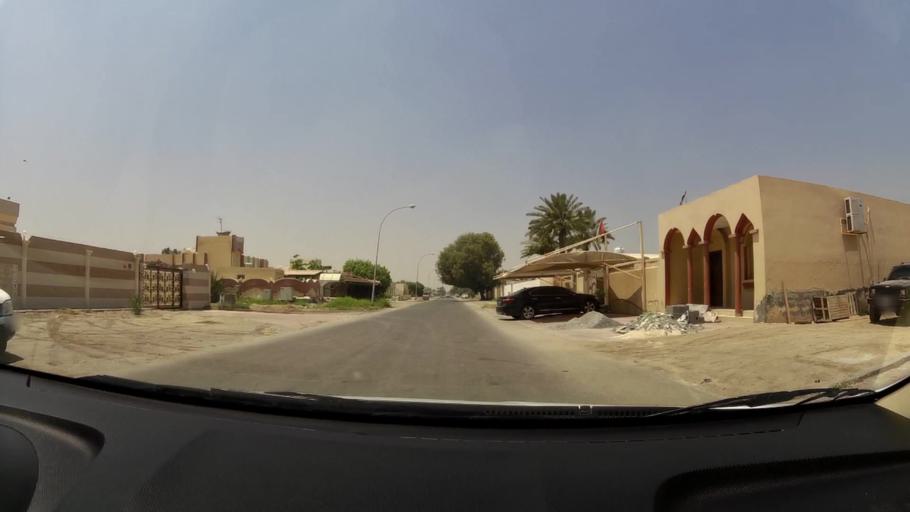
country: AE
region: Umm al Qaywayn
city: Umm al Qaywayn
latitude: 25.5529
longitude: 55.5584
